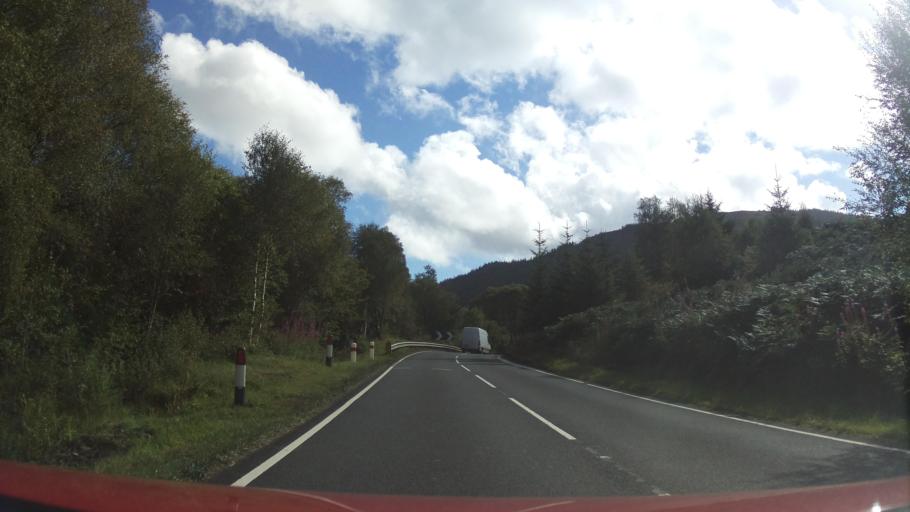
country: GB
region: Scotland
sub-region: Stirling
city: Callander
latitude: 56.4156
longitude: -4.5083
